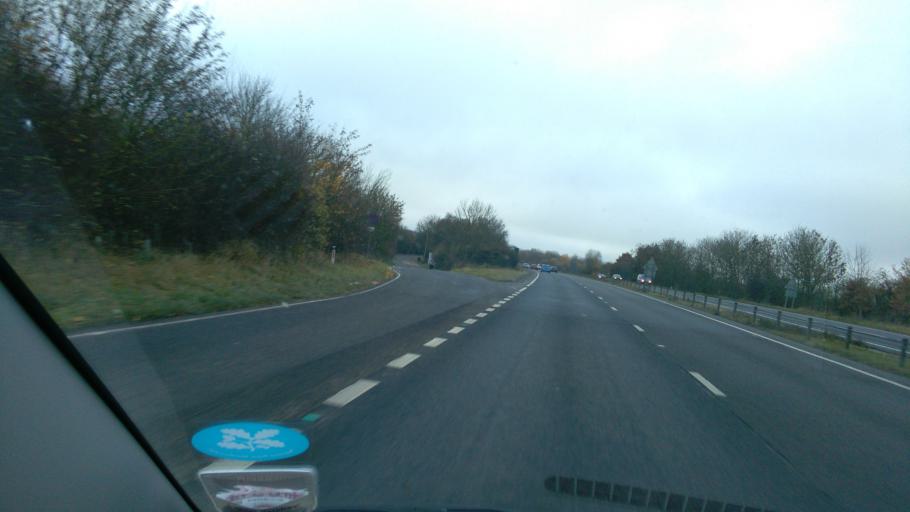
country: GB
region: England
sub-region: Northamptonshire
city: Towcester
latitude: 52.1224
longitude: -1.0061
